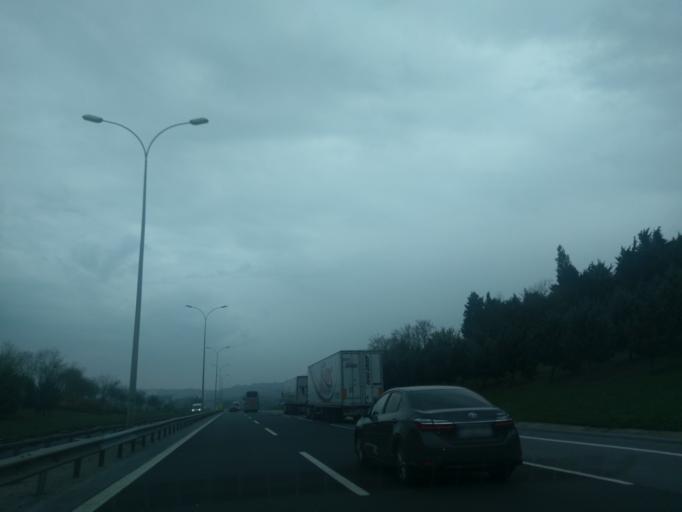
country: TR
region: Istanbul
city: Bueyuekcekmece
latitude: 41.1047
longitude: 28.5870
